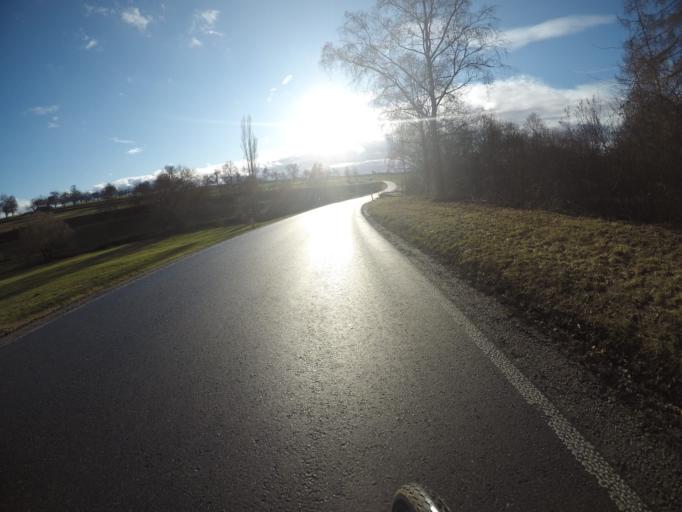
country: DE
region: Baden-Wuerttemberg
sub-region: Regierungsbezirk Stuttgart
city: Bondorf
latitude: 48.5355
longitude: 8.8770
